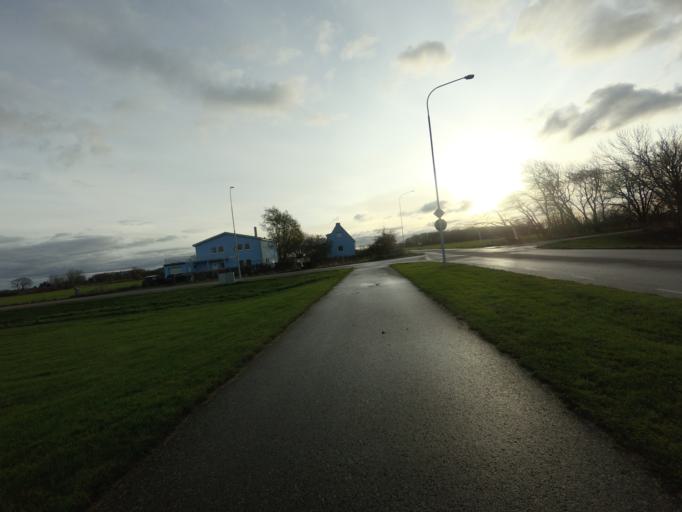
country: SE
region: Skane
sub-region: Hoganas Kommun
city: Hoganas
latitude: 56.1890
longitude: 12.5839
